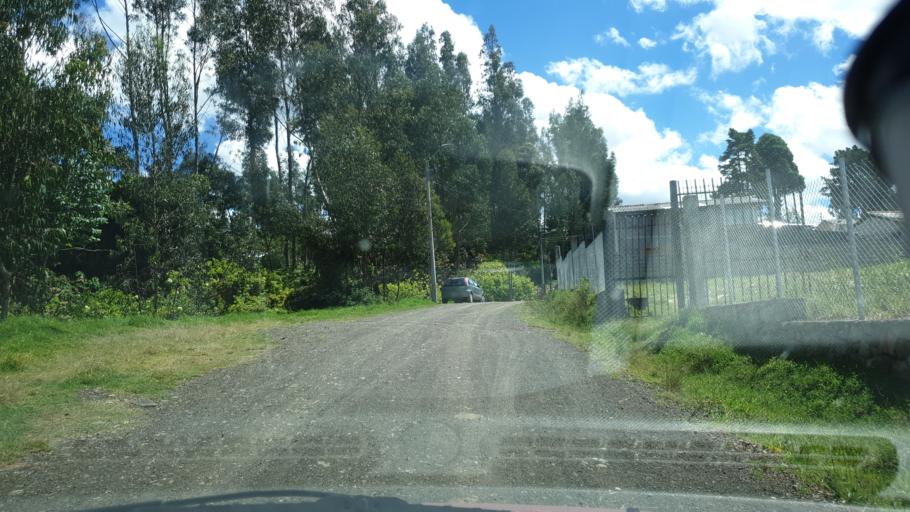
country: EC
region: Azuay
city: Cuenca
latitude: -2.8746
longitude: -78.9516
